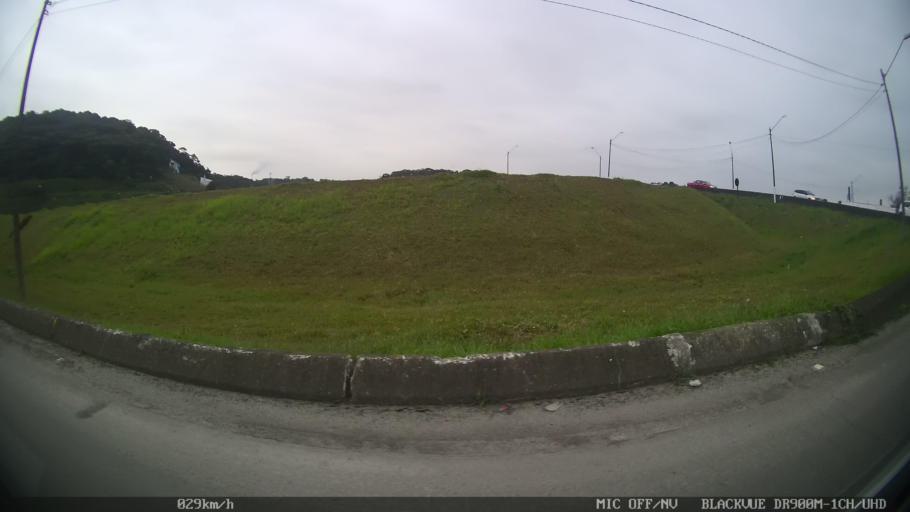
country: BR
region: Santa Catarina
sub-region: Joinville
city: Joinville
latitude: -26.4383
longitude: -48.8076
